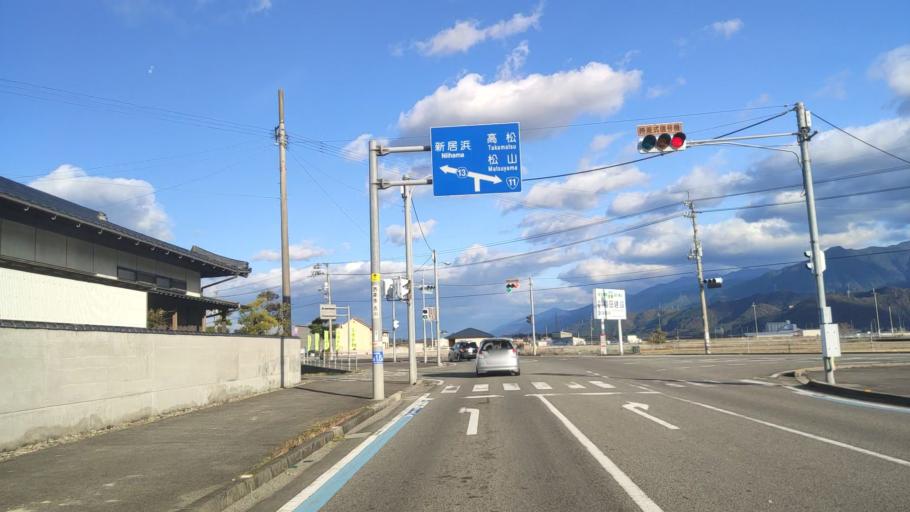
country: JP
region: Ehime
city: Saijo
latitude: 33.9088
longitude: 133.1563
